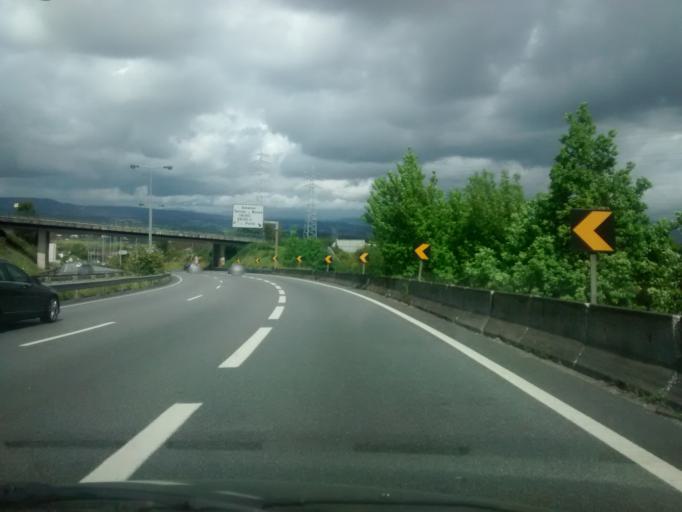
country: PT
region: Braga
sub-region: Braga
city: Braga
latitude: 41.5692
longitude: -8.4222
